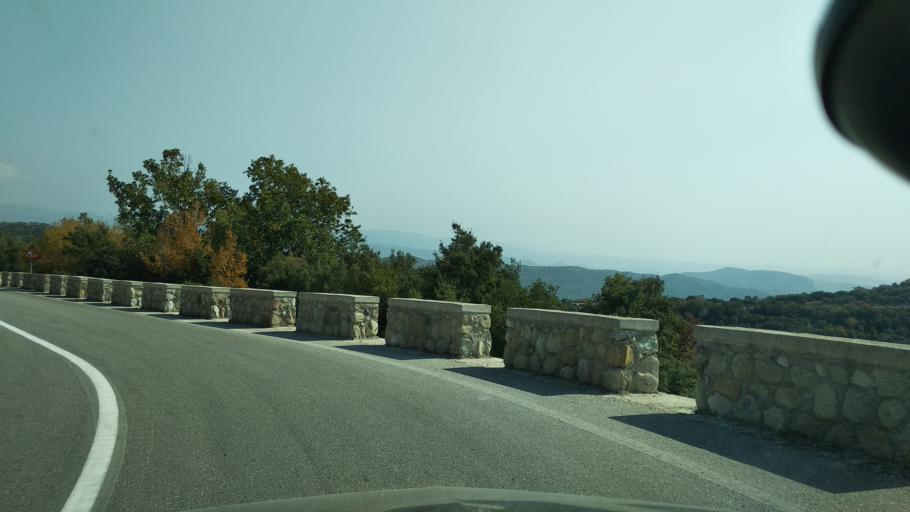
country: GR
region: Thessaly
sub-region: Trikala
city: Kalampaka
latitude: 39.7180
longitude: 21.6379
